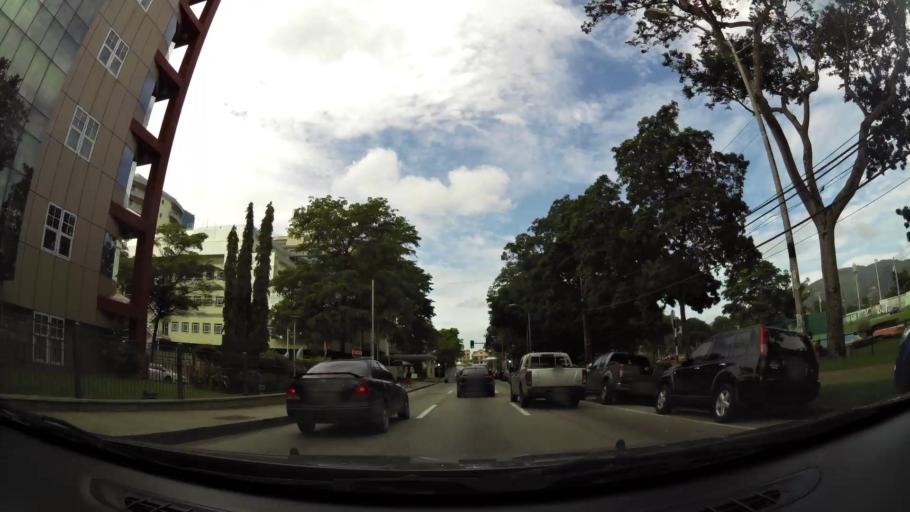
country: TT
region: City of Port of Spain
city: Port-of-Spain
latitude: 10.6642
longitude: -61.5139
